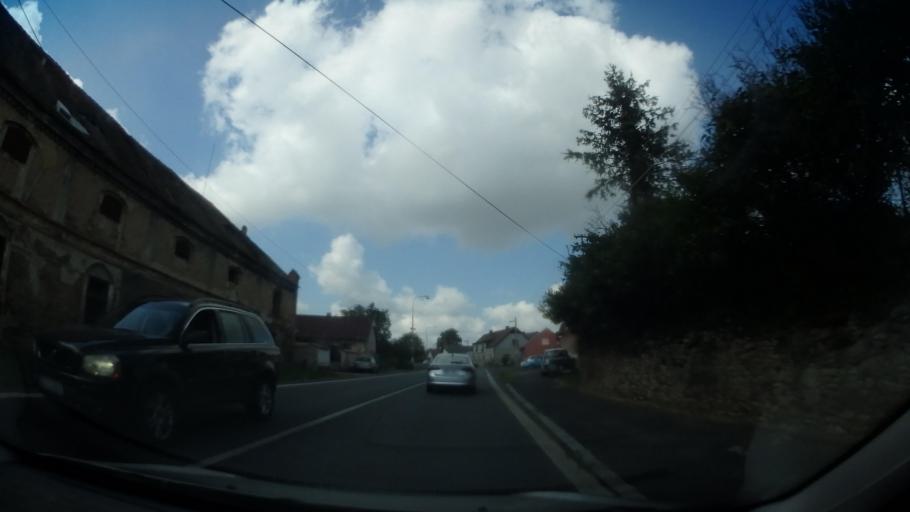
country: CZ
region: Central Bohemia
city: Cervene Pecky
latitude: 49.9465
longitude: 15.2038
